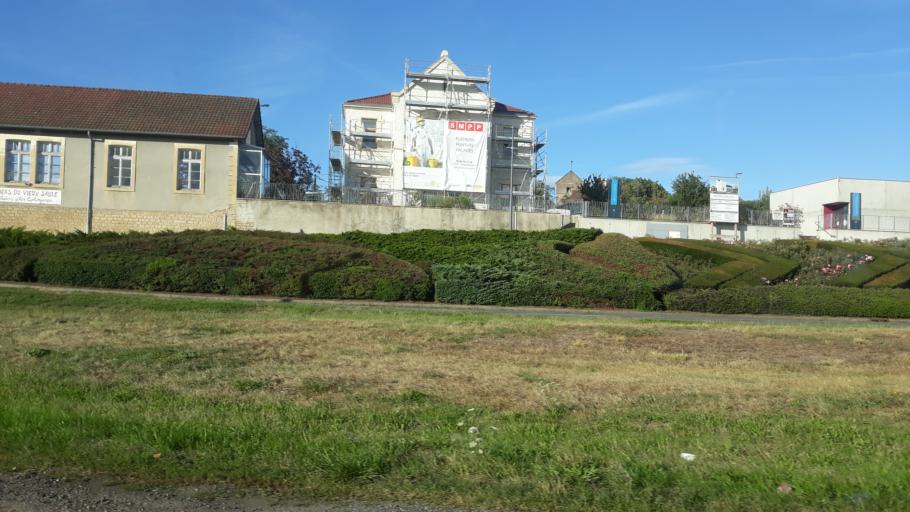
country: FR
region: Bourgogne
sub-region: Departement de Saone-et-Loire
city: Torcy
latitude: 46.7686
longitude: 4.4515
